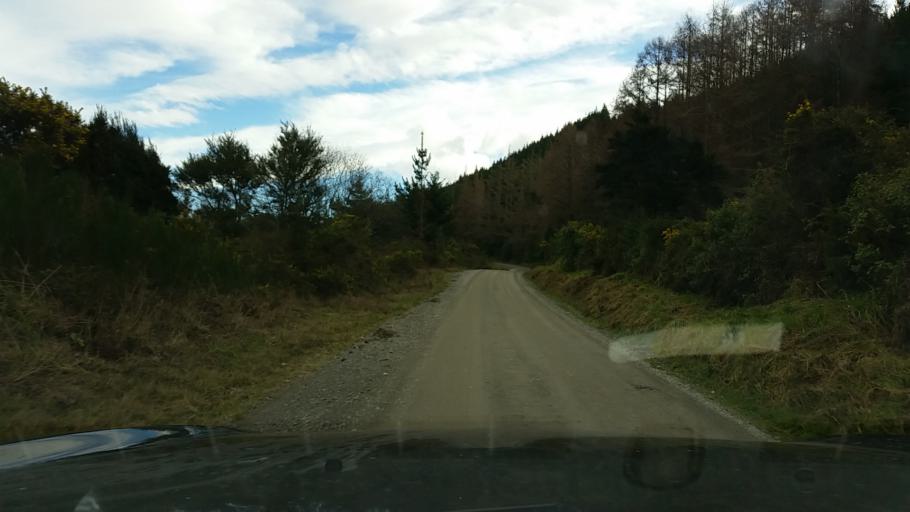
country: NZ
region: Nelson
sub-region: Nelson City
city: Nelson
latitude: -41.5773
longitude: 173.4343
